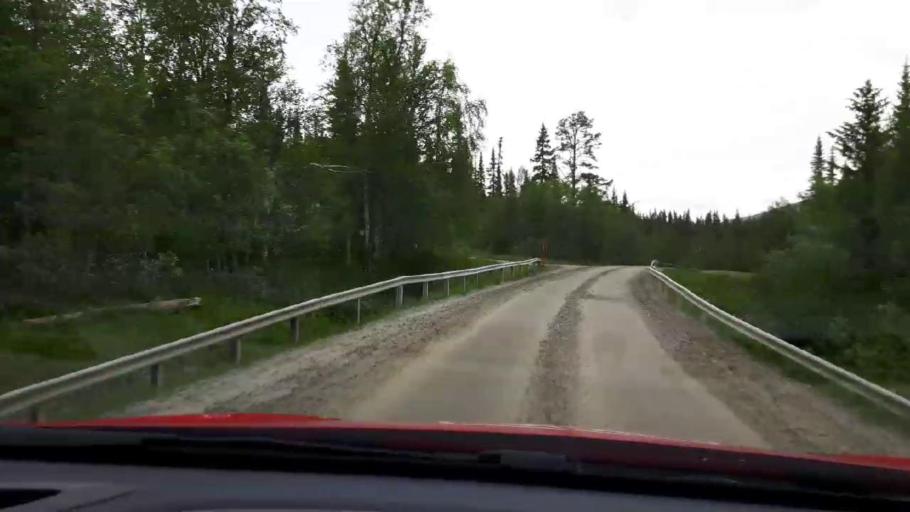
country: SE
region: Jaemtland
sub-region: Are Kommun
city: Are
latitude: 62.8469
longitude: 12.7893
